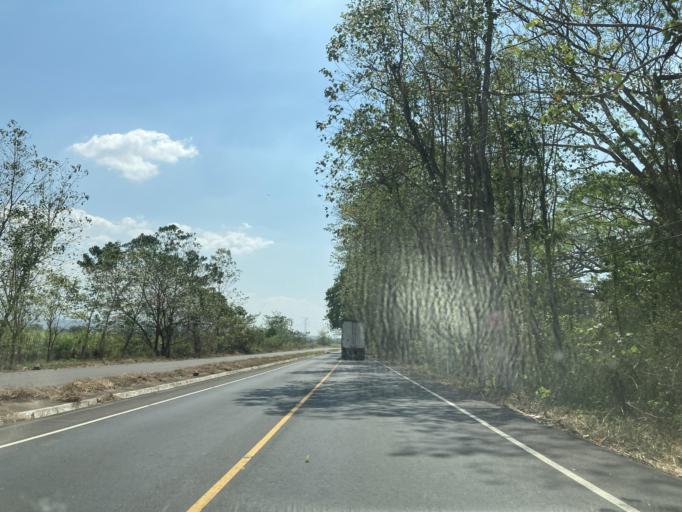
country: GT
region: Escuintla
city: Guanagazapa
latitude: 14.2001
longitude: -90.7016
